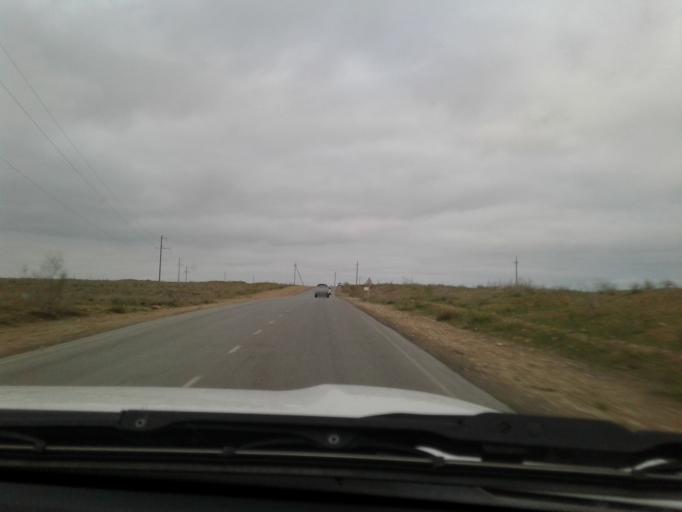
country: TM
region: Lebap
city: Farap
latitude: 39.0941
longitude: 63.7201
